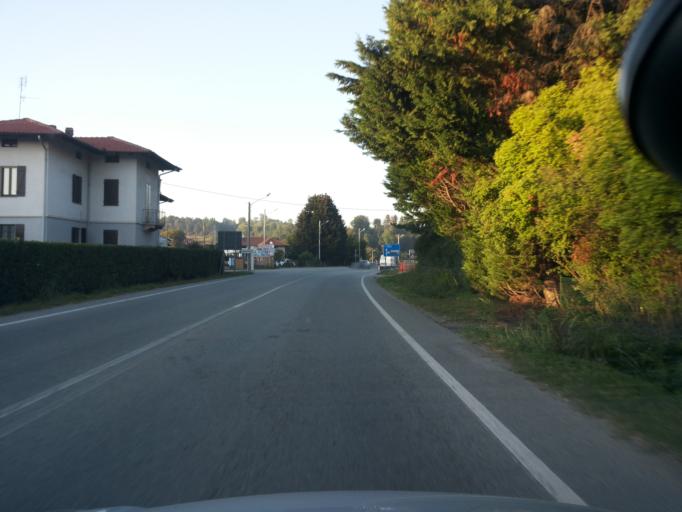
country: IT
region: Piedmont
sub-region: Provincia di Biella
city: Dorzano
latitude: 45.4217
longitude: 8.0998
